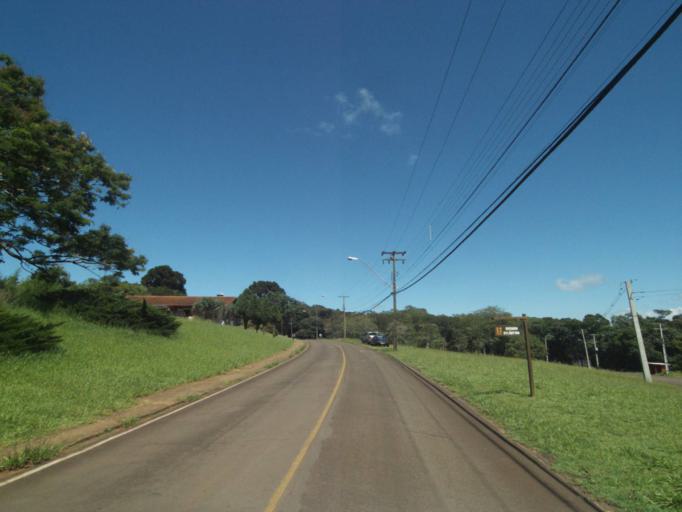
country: BR
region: Parana
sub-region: Pinhao
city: Pinhao
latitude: -25.7921
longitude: -52.0879
